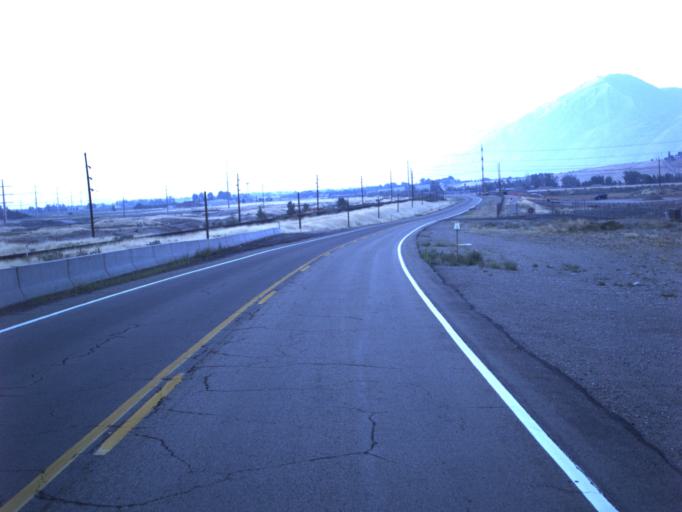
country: US
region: Utah
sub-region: Utah County
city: Mapleton
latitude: 40.0859
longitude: -111.5896
